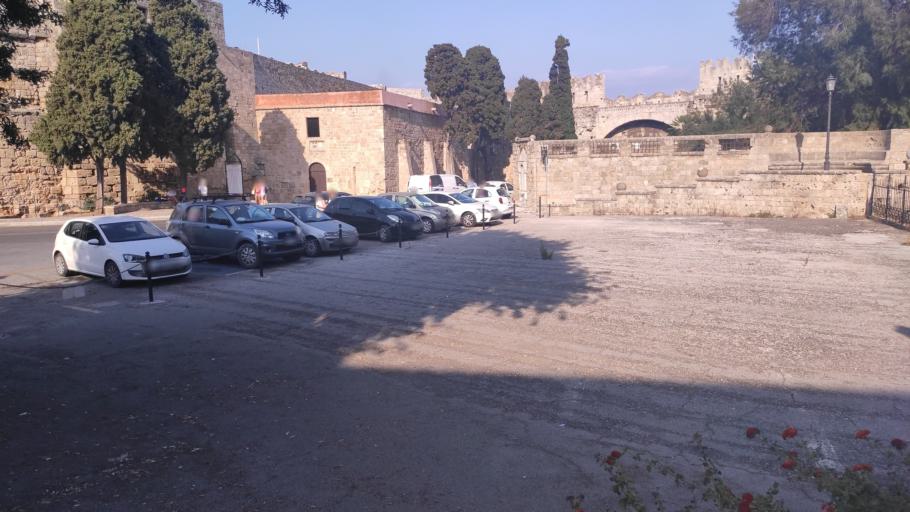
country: GR
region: South Aegean
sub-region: Nomos Dodekanisou
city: Rodos
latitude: 36.4461
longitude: 28.2272
